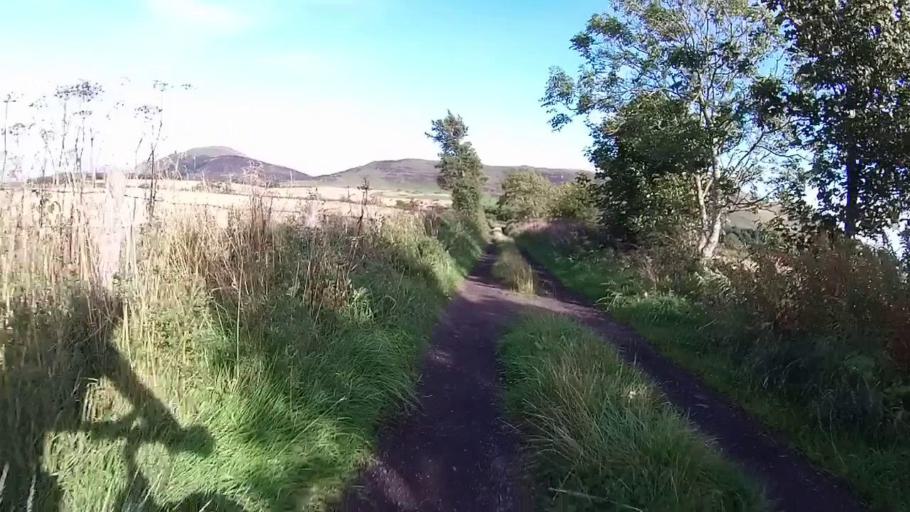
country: GB
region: Scotland
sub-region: Perth and Kinross
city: Milnathort
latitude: 56.2348
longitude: -3.3485
